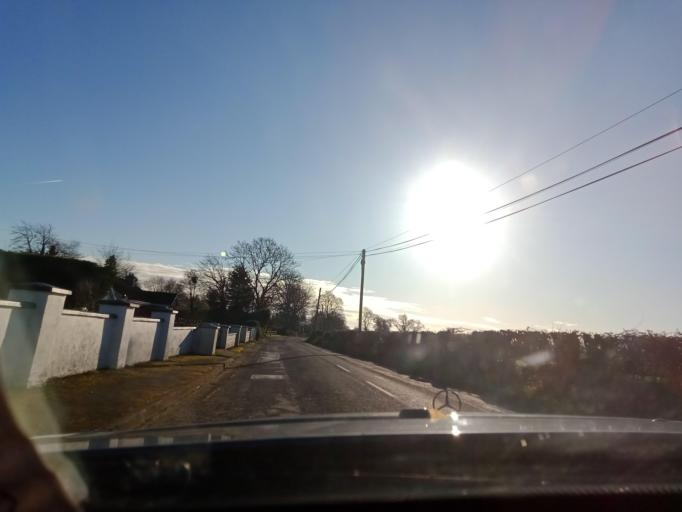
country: IE
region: Leinster
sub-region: Kilkenny
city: Piltown
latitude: 52.3857
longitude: -7.3449
